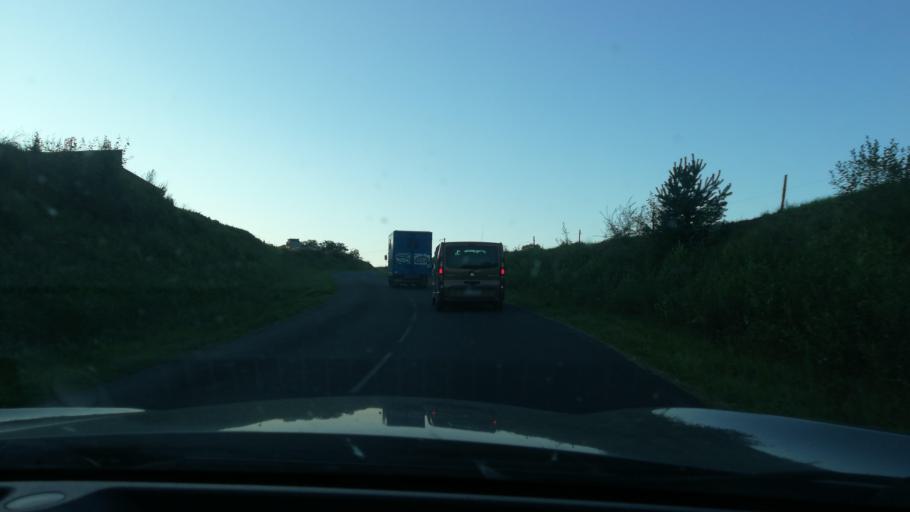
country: FR
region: Auvergne
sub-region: Departement du Cantal
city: Laroquebrou
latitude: 44.9357
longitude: 2.0829
